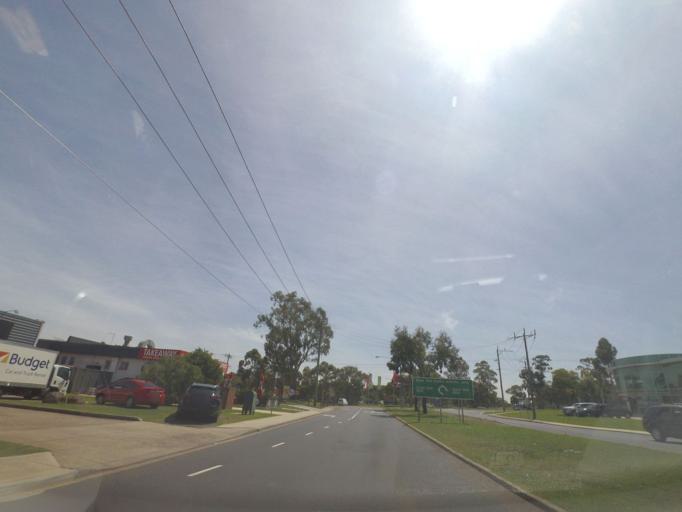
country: AU
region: Victoria
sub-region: Brimbank
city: Keilor Park
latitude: -37.7135
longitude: 144.8604
